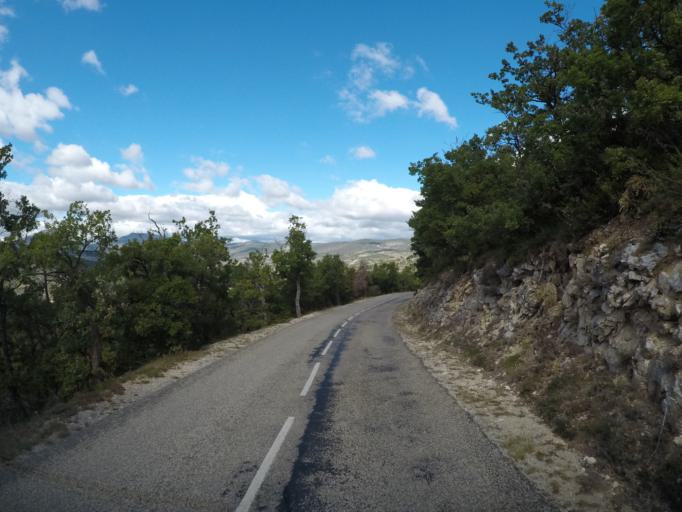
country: FR
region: Provence-Alpes-Cote d'Azur
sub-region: Departement du Vaucluse
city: Sault
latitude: 44.1604
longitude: 5.4412
